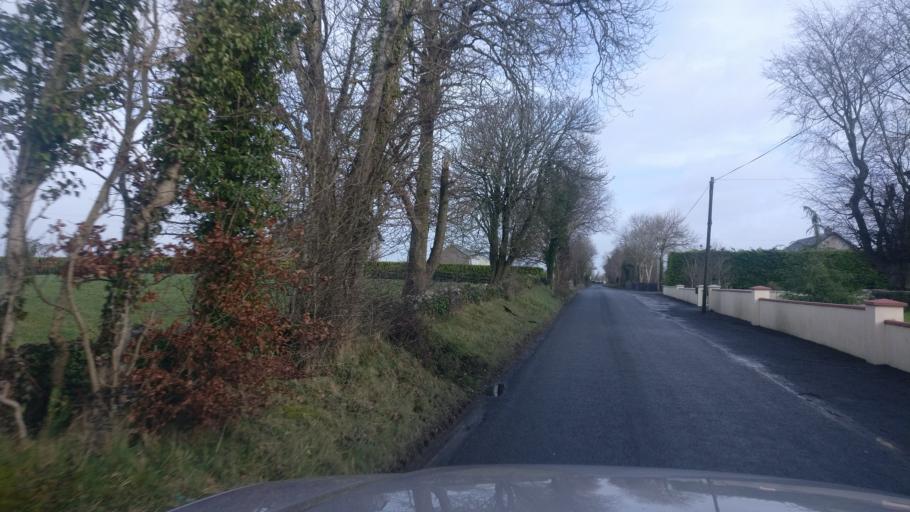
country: IE
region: Connaught
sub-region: County Galway
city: Loughrea
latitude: 53.2735
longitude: -8.5881
